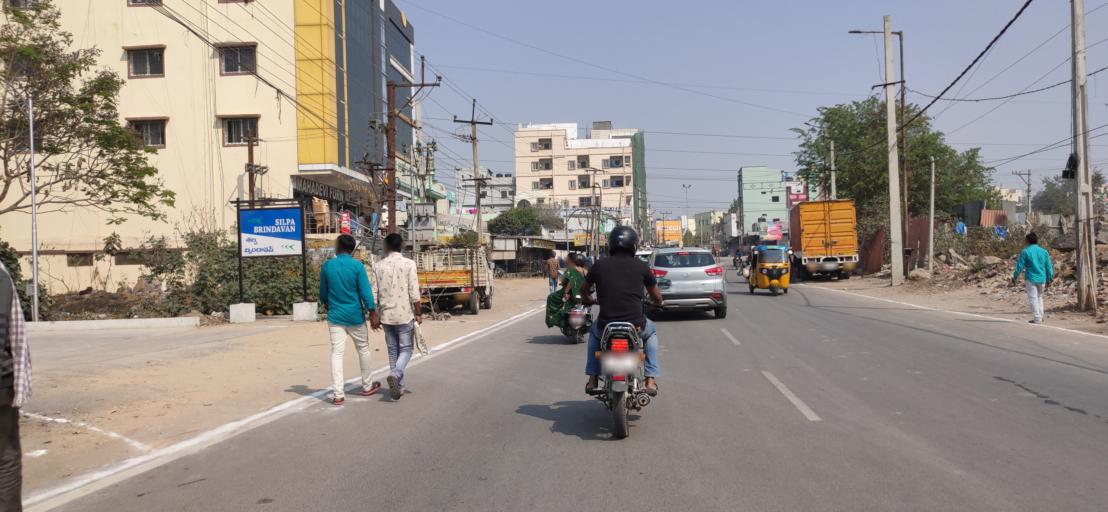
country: IN
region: Telangana
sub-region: Rangareddi
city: Kukatpalli
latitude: 17.5064
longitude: 78.4077
